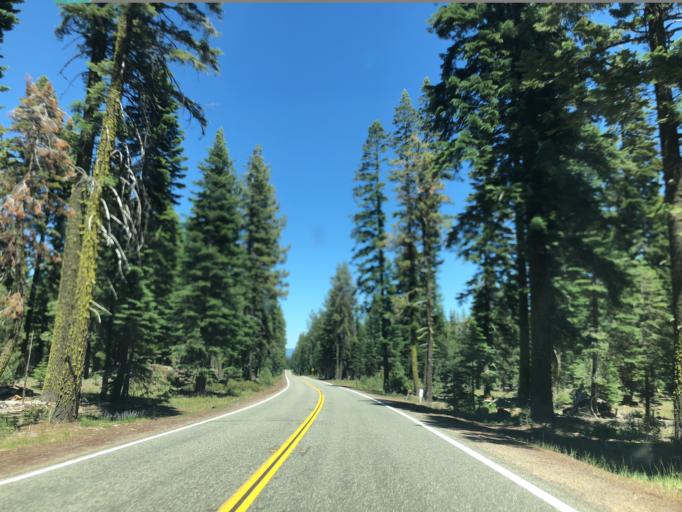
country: US
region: California
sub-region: Shasta County
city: Burney
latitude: 40.5817
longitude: -121.5589
